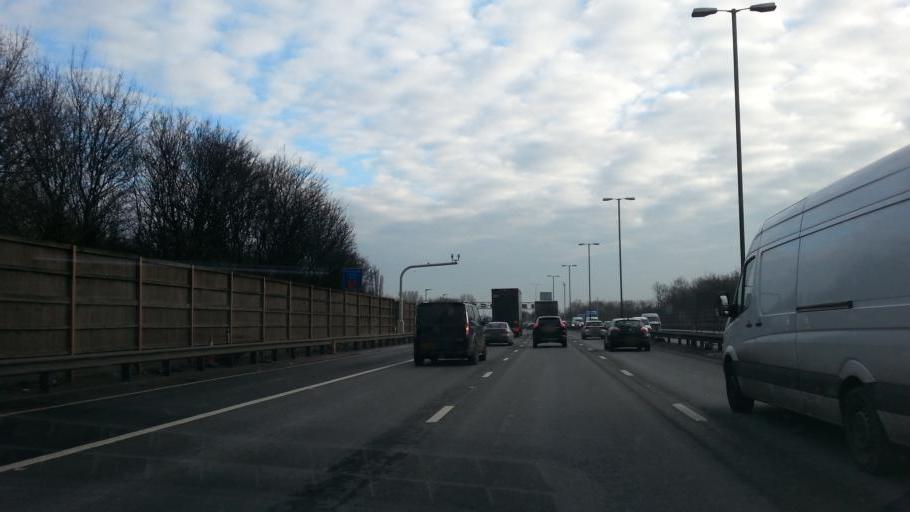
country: GB
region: England
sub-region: City and Borough of Birmingham
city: Hockley
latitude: 52.5417
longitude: -1.9130
